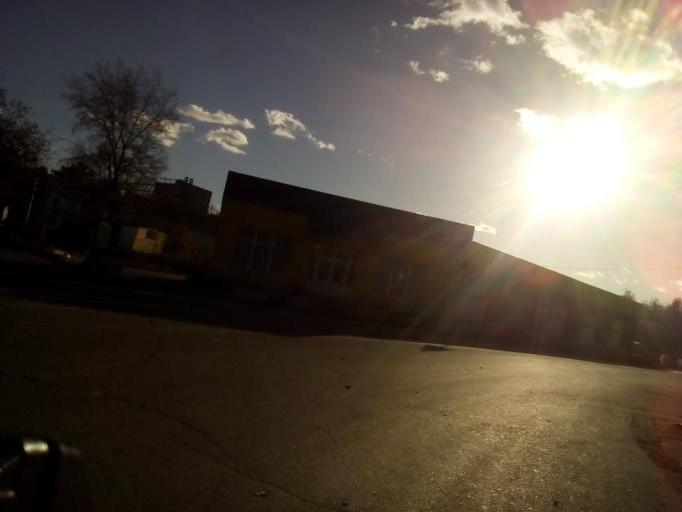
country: RU
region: Moscow
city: Zapadnoye Degunino
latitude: 55.8460
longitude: 37.5410
